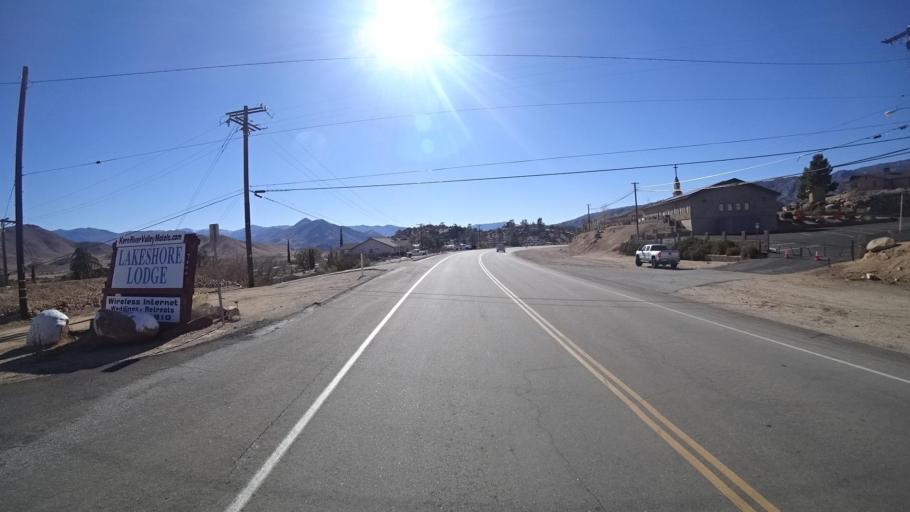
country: US
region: California
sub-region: Kern County
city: Wofford Heights
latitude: 35.7107
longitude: -118.4429
